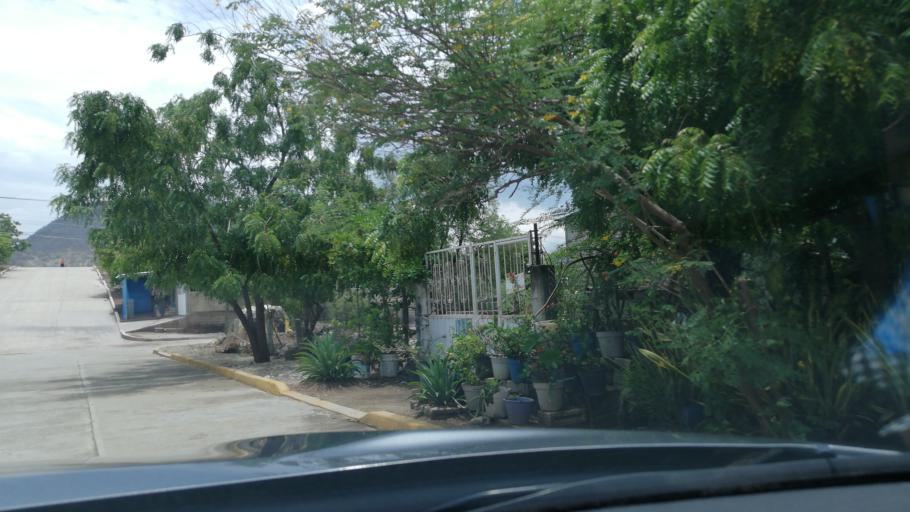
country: MX
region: Oaxaca
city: Santa Maria Jalapa del Marques
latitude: 16.4433
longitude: -95.4402
